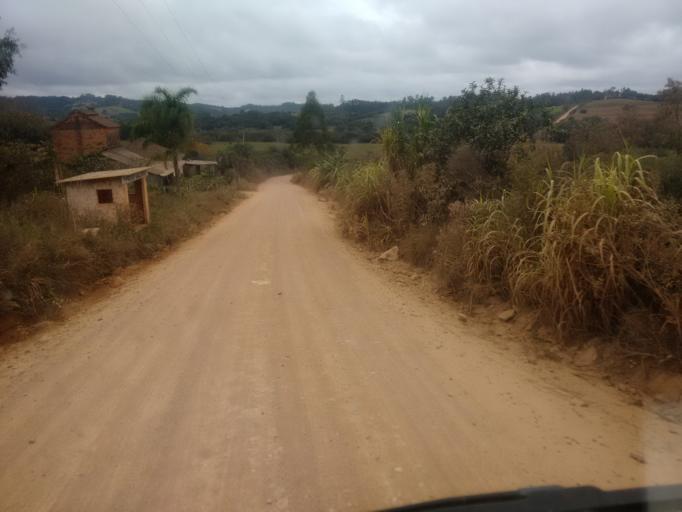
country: BR
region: Rio Grande do Sul
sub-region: Camaqua
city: Camaqua
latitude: -30.7586
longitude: -51.8708
